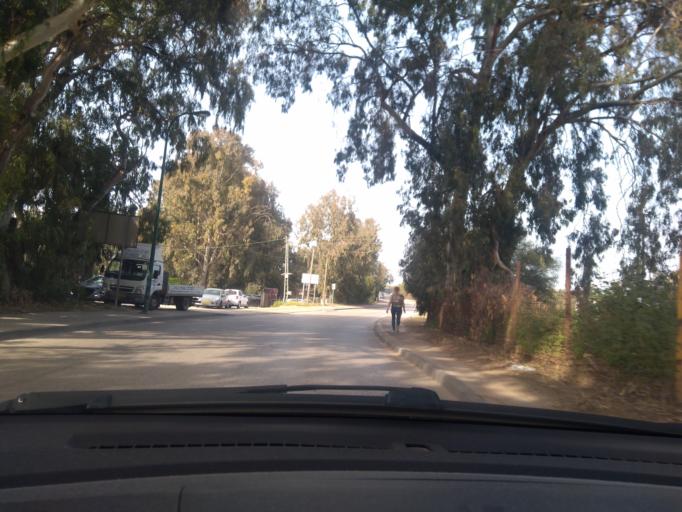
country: IL
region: Central District
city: Netanya
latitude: 32.3224
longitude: 34.8683
